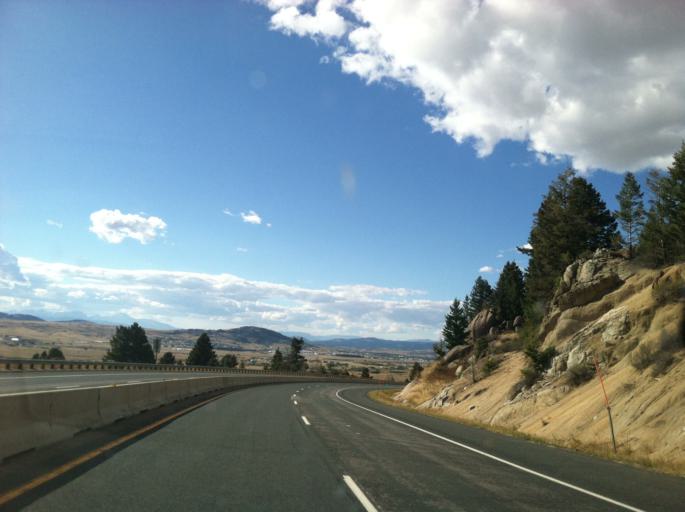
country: US
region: Montana
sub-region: Silver Bow County
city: Butte
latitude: 45.9291
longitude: -112.4464
